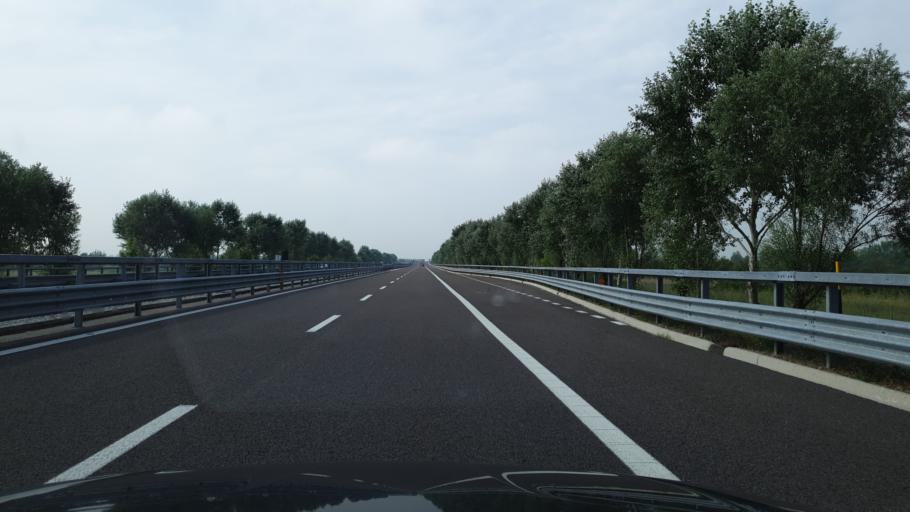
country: IT
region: Veneto
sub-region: Provincia di Padova
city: Megliadino San Vitale
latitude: 45.1693
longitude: 11.5341
